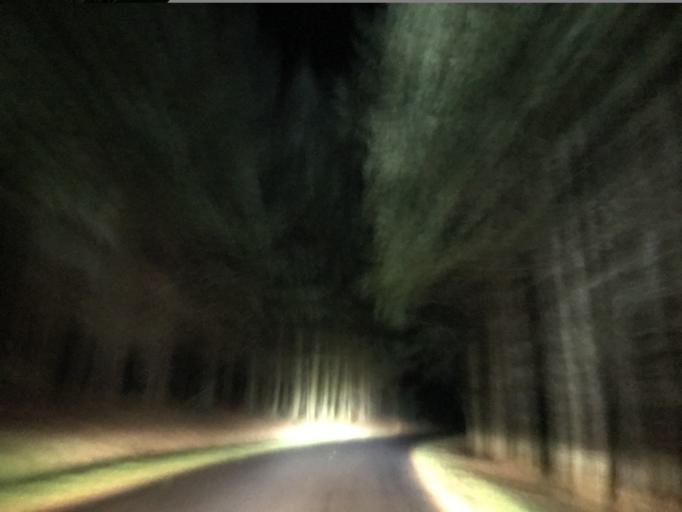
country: FR
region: Auvergne
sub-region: Departement du Puy-de-Dome
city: Saint-Remy-sur-Durolle
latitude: 45.9609
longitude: 3.6374
